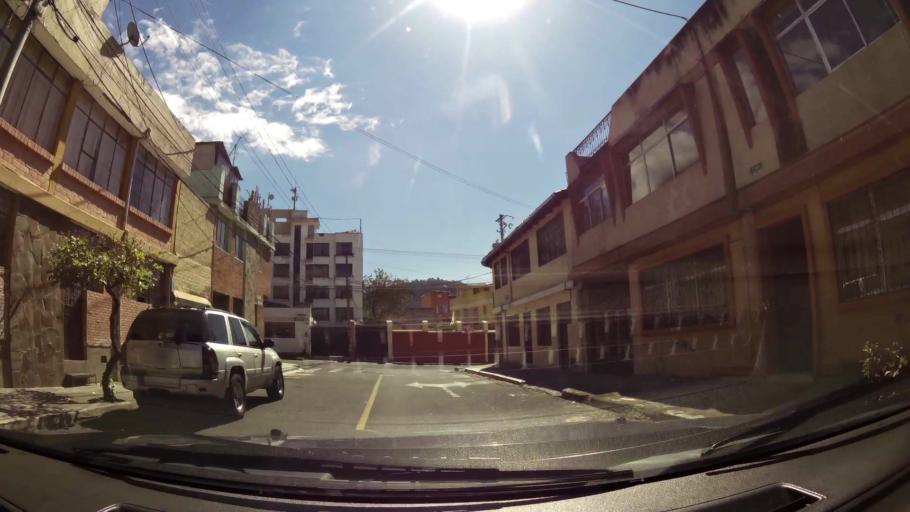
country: EC
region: Pichincha
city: Quito
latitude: -0.2396
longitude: -78.5284
